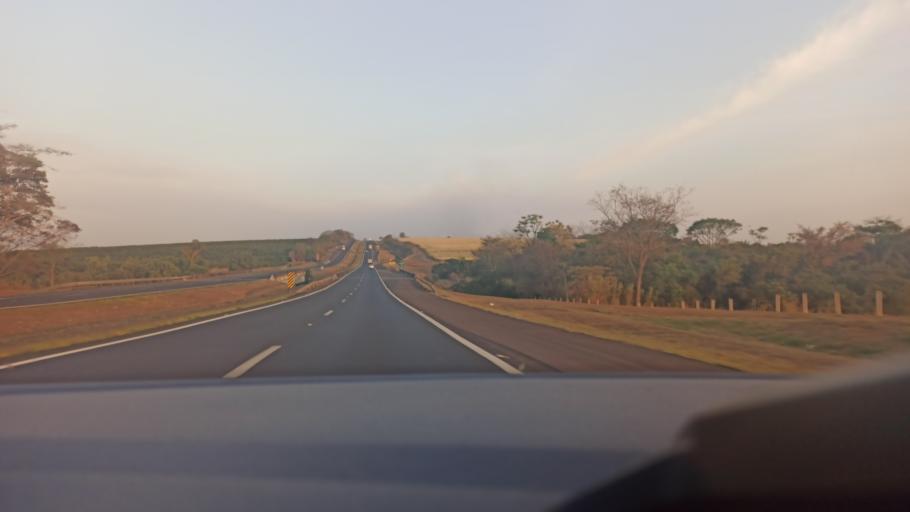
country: BR
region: Sao Paulo
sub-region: Taquaritinga
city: Taquaritinga
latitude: -21.4329
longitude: -48.6606
